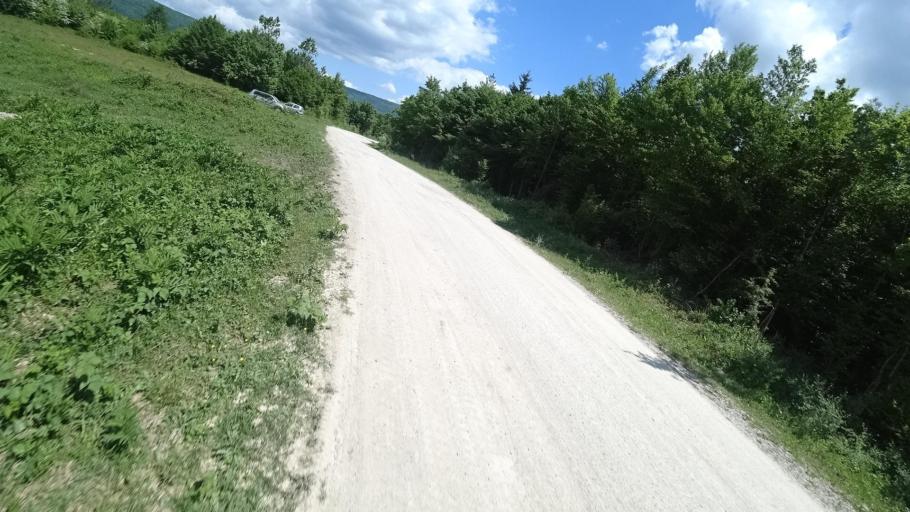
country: BA
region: Federation of Bosnia and Herzegovina
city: Bihac
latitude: 44.8330
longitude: 15.9226
